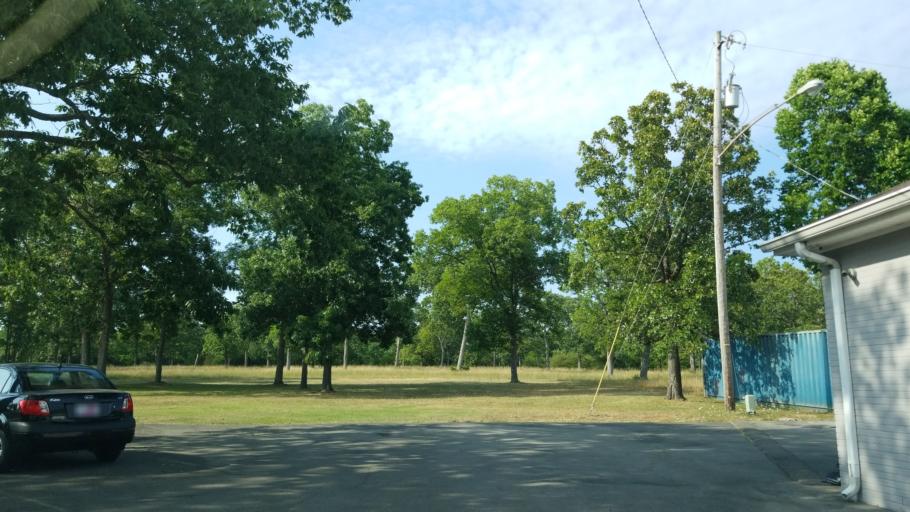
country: US
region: Tennessee
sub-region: Rutherford County
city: La Vergne
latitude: 36.0468
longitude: -86.5834
